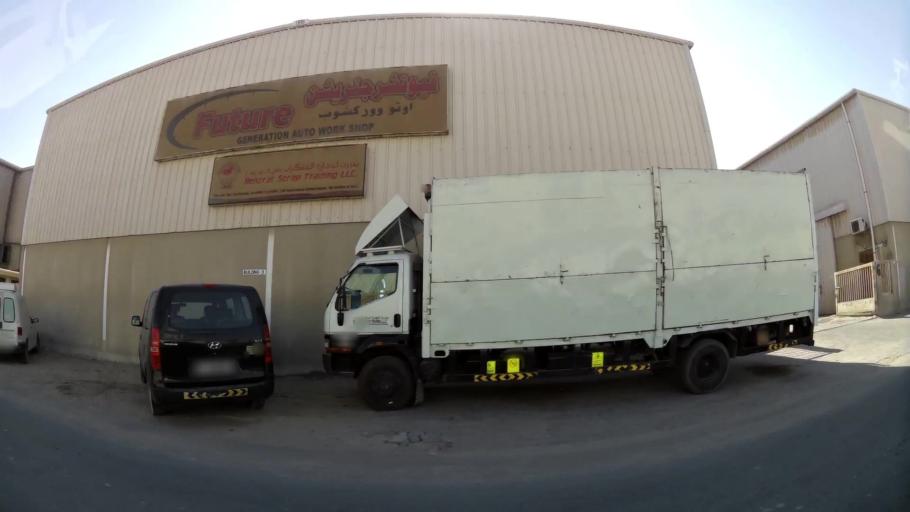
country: AE
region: Dubai
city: Dubai
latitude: 24.9898
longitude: 55.0985
